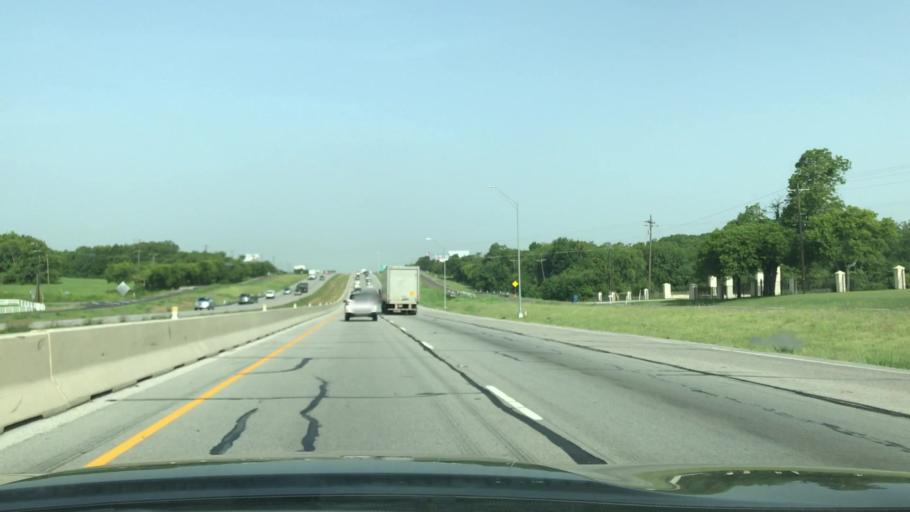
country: US
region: Texas
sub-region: Dallas County
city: Sunnyvale
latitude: 32.7816
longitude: -96.5417
